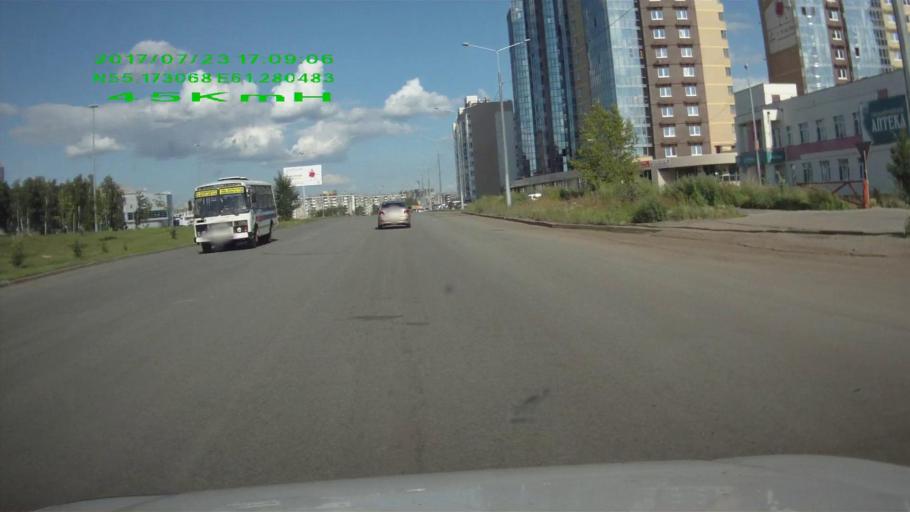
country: RU
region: Chelyabinsk
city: Roshchino
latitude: 55.1727
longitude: 61.2815
